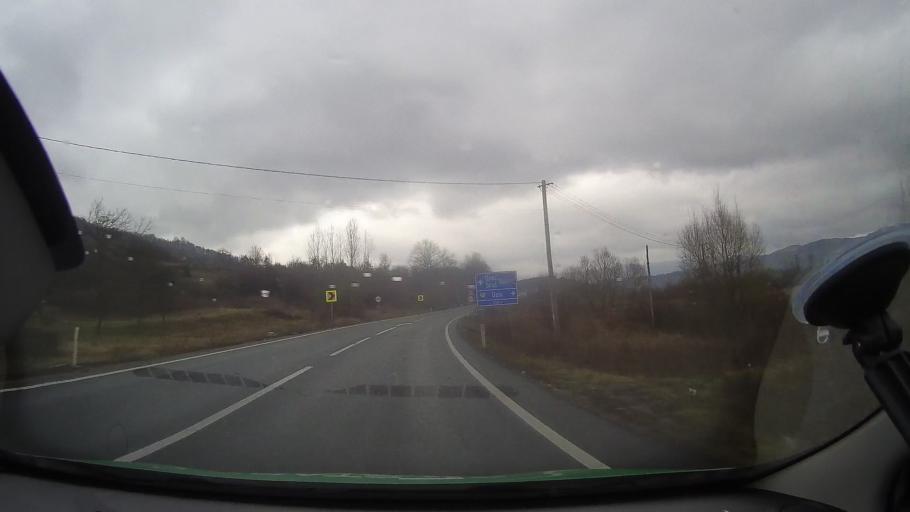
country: RO
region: Hunedoara
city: Vata de Jos
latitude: 46.2123
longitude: 22.5796
